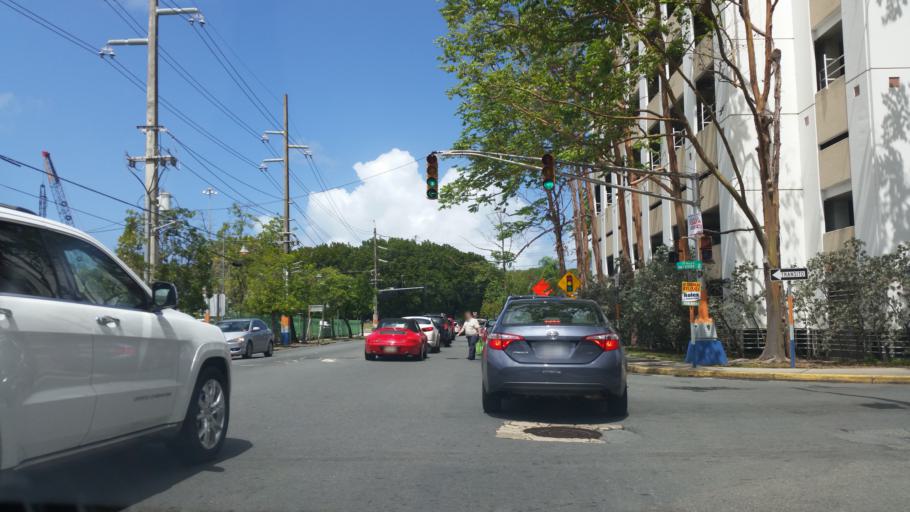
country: PR
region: Catano
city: Catano
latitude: 18.4096
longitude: -66.1038
